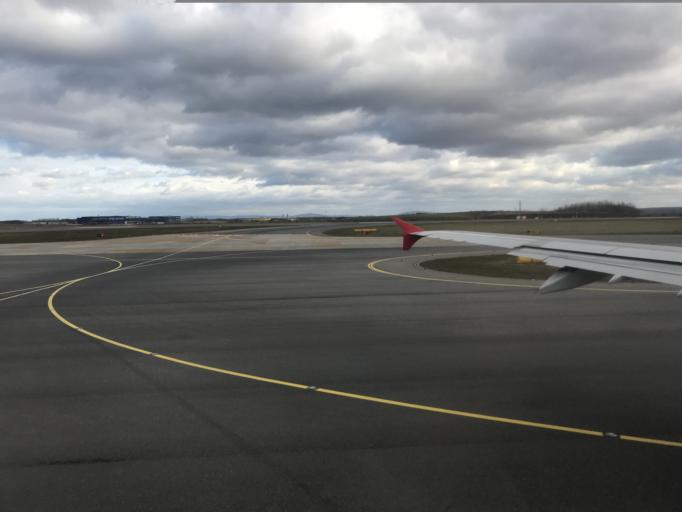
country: AT
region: Lower Austria
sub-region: Politischer Bezirk Wien-Umgebung
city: Fischamend Dorf
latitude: 48.1180
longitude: 16.5744
